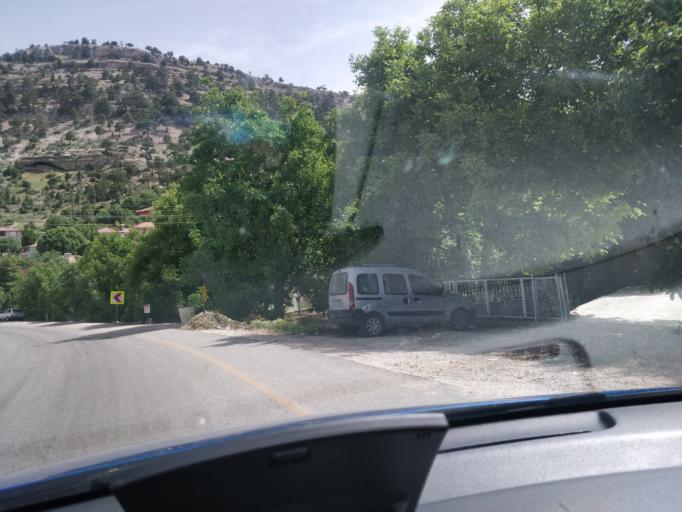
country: TR
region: Karaman
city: Bucakkisla
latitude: 36.8824
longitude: 33.2813
